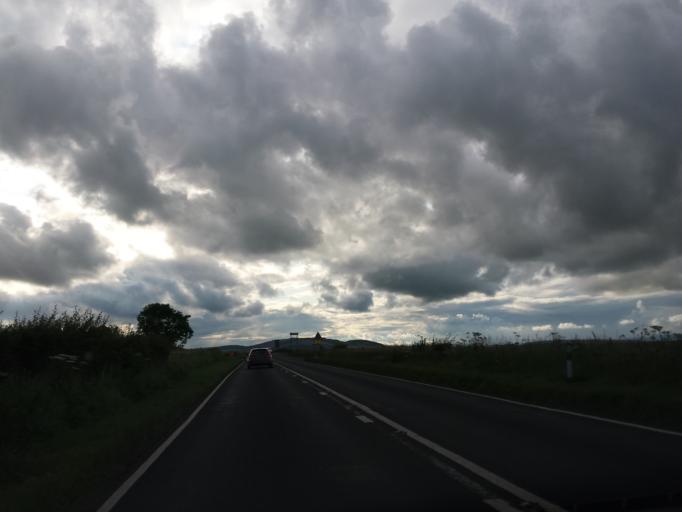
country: GB
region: Scotland
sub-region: Fife
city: Strathkinness
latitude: 56.3562
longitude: -2.8588
